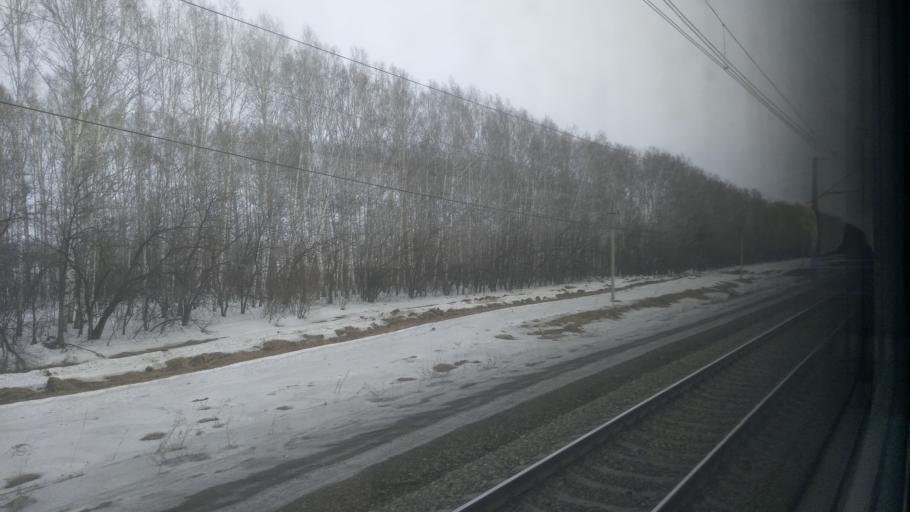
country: RU
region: Novosibirsk
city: Bolotnoye
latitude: 55.6946
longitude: 84.5402
